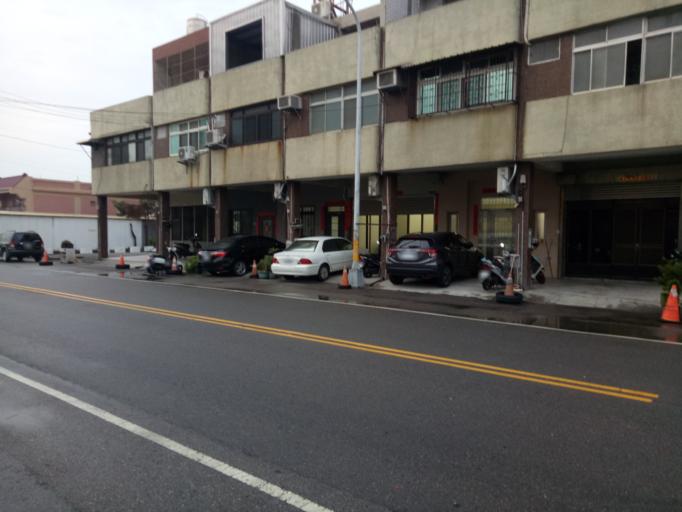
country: TW
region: Taiwan
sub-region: Taichung City
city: Taichung
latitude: 24.2462
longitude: 120.5417
